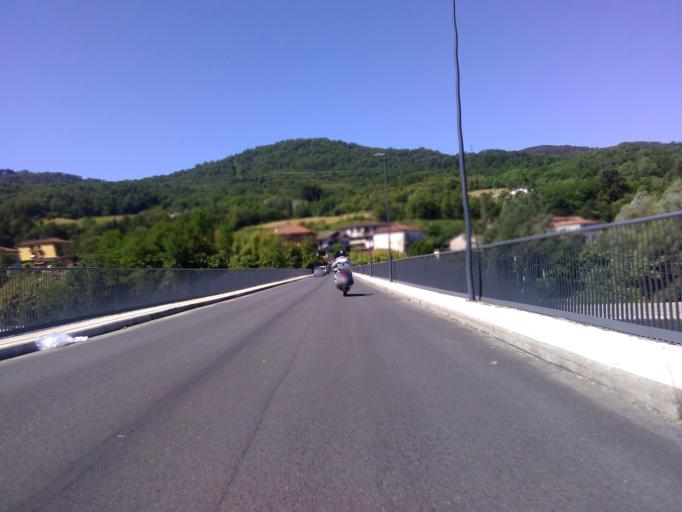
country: IT
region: Tuscany
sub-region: Provincia di Massa-Carrara
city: Villafranca in Lunigiana
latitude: 44.2937
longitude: 9.9430
